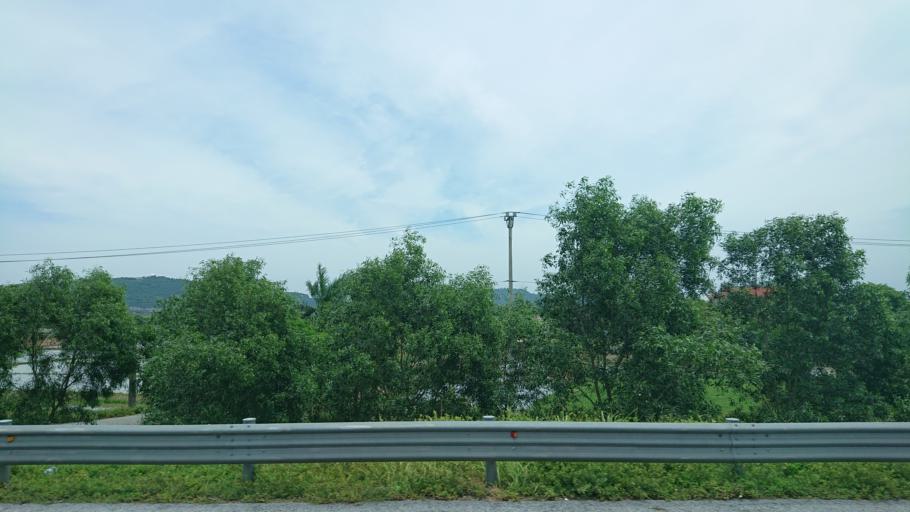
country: VN
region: Hai Phong
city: Nui Doi
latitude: 20.7704
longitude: 106.6227
